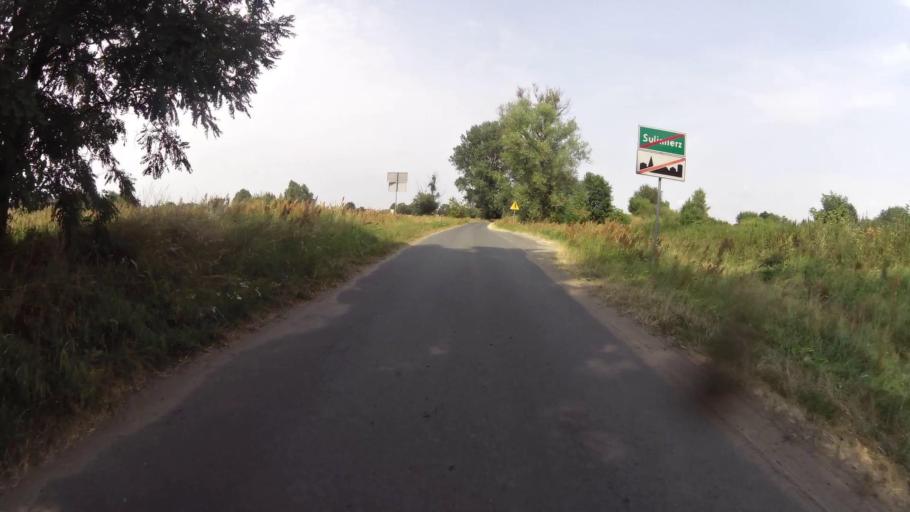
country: PL
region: West Pomeranian Voivodeship
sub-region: Powiat mysliborski
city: Nowogrodek Pomorski
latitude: 52.9679
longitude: 15.0216
